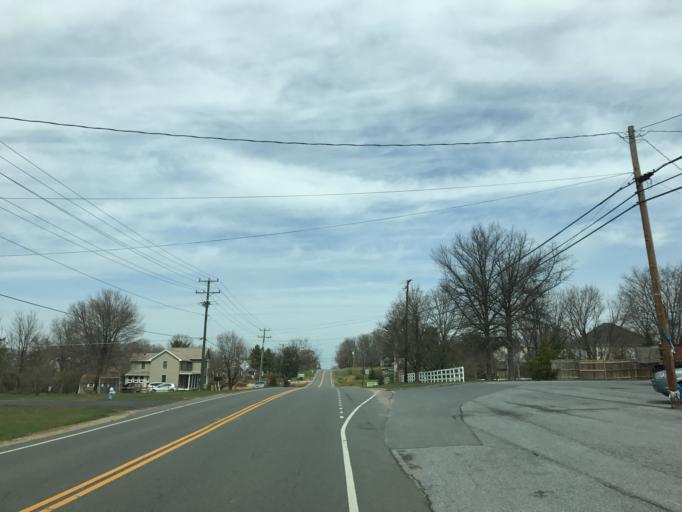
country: US
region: Virginia
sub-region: Loudoun County
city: Lovettsville
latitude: 39.2783
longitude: -77.6382
